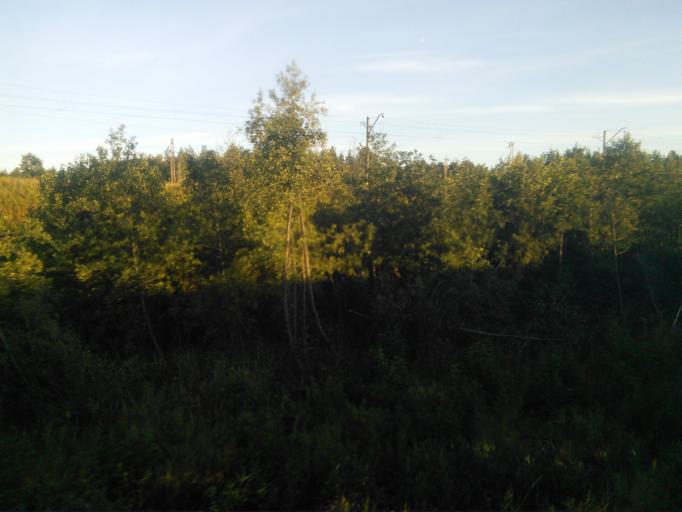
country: RU
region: Moskovskaya
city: Fryazevo
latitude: 55.7368
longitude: 38.4793
